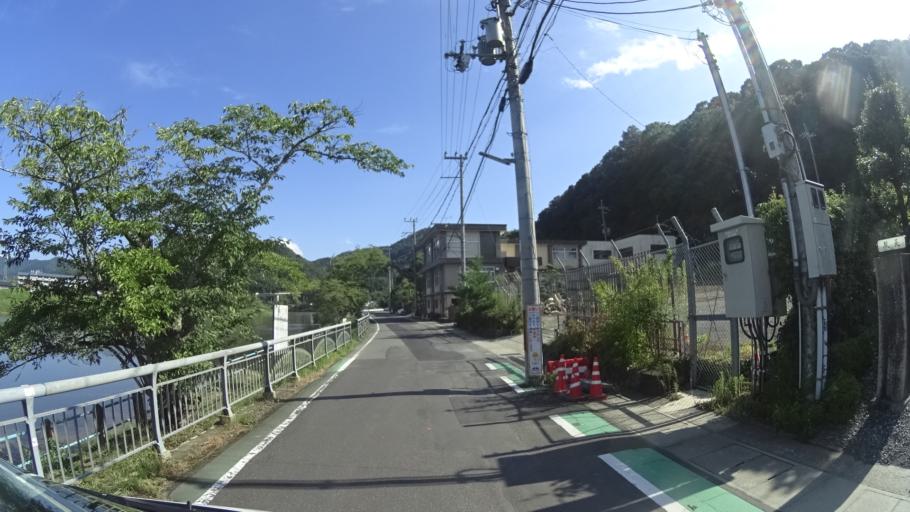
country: JP
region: Kyoto
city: Ayabe
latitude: 35.2950
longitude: 135.2636
